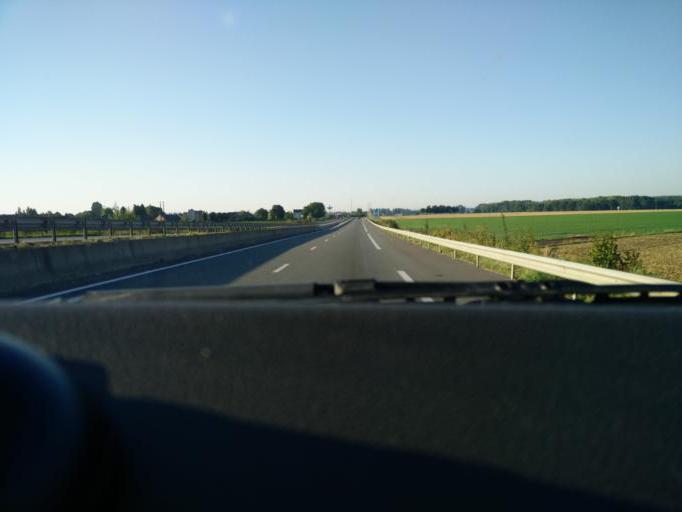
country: FR
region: Nord-Pas-de-Calais
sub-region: Departement du Nord
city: Salome
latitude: 50.5384
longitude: 2.8330
